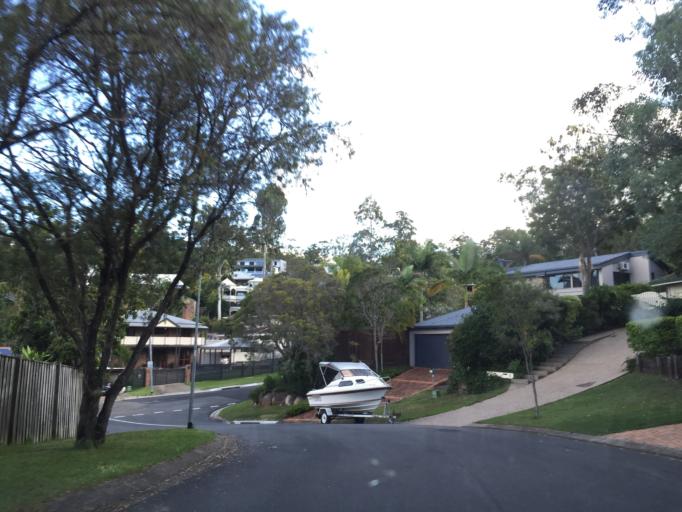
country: AU
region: Queensland
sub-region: Moreton Bay
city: Ferny Hills
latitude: -27.4389
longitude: 152.9288
